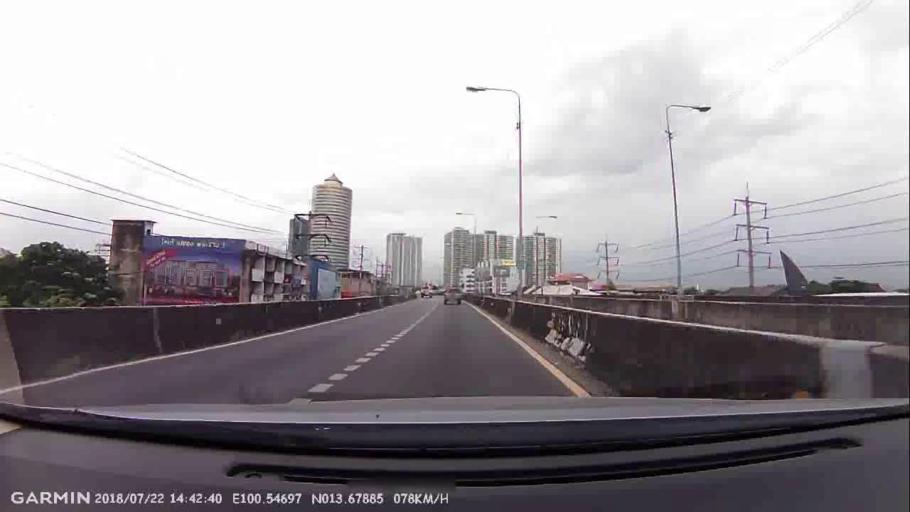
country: TH
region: Bangkok
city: Yan Nawa
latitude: 13.6790
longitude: 100.5465
